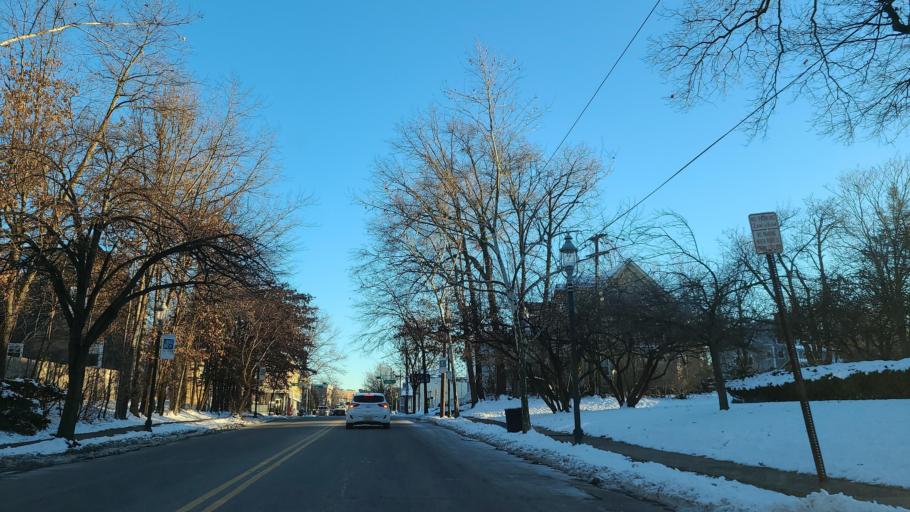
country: US
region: New Jersey
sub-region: Essex County
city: South Orange
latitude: 40.7428
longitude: -74.2549
